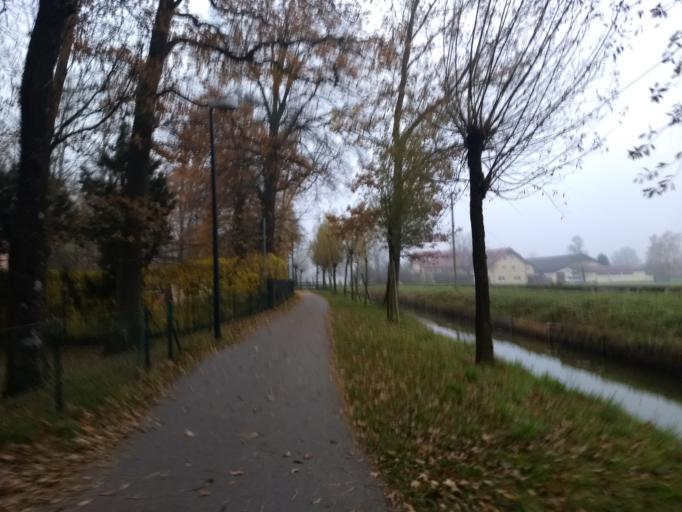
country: AT
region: Salzburg
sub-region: Salzburg Stadt
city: Salzburg
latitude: 47.7709
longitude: 13.0385
